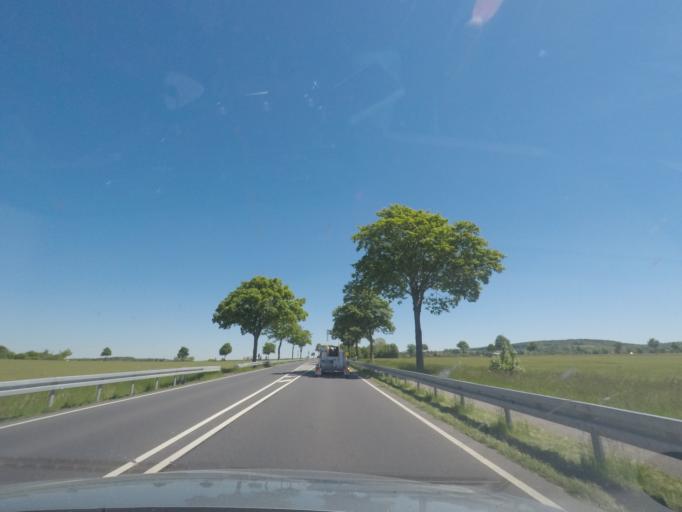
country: DE
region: Lower Saxony
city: Veltheim
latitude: 52.2467
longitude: 10.6992
